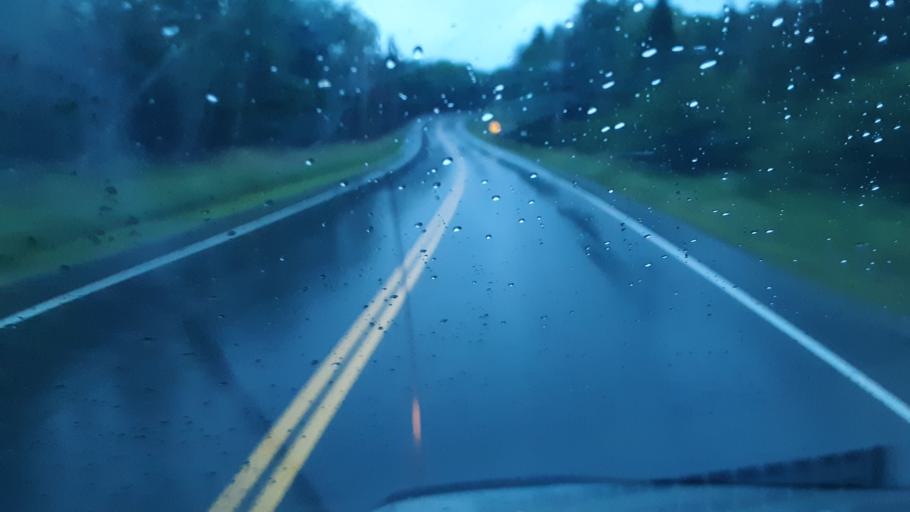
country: US
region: Maine
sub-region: Penobscot County
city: Patten
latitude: 45.8874
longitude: -68.4221
